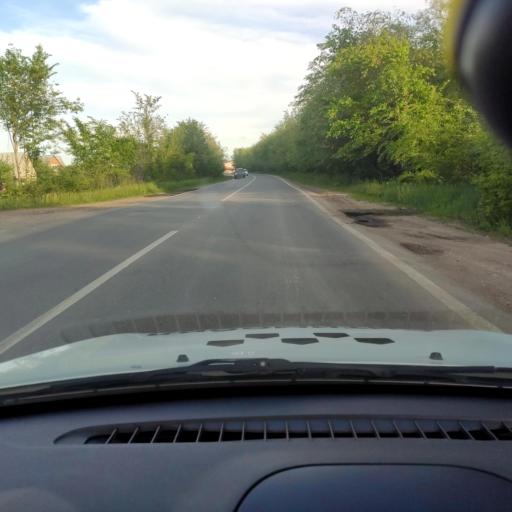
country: RU
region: Samara
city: Podstepki
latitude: 53.5869
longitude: 49.0526
